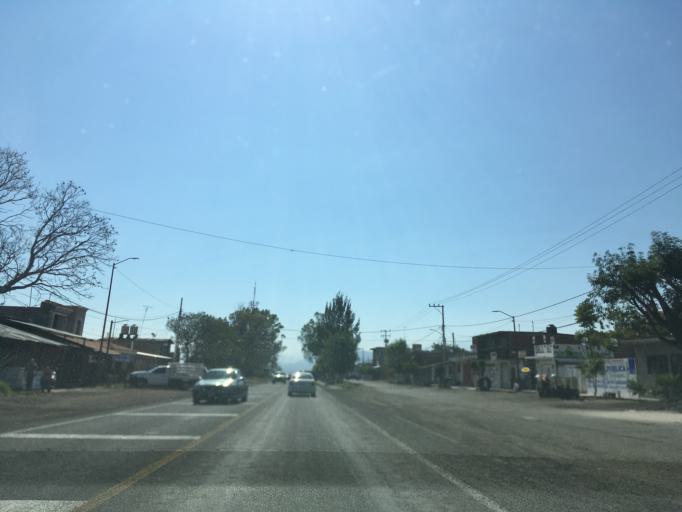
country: MX
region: Michoacan
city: Indaparapeo
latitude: 19.7916
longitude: -100.9671
